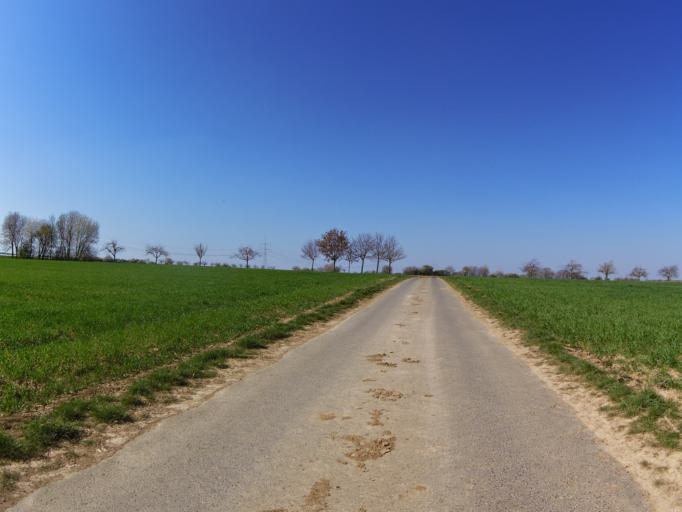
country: DE
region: Bavaria
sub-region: Regierungsbezirk Unterfranken
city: Biebelried
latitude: 49.8174
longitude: 10.0932
